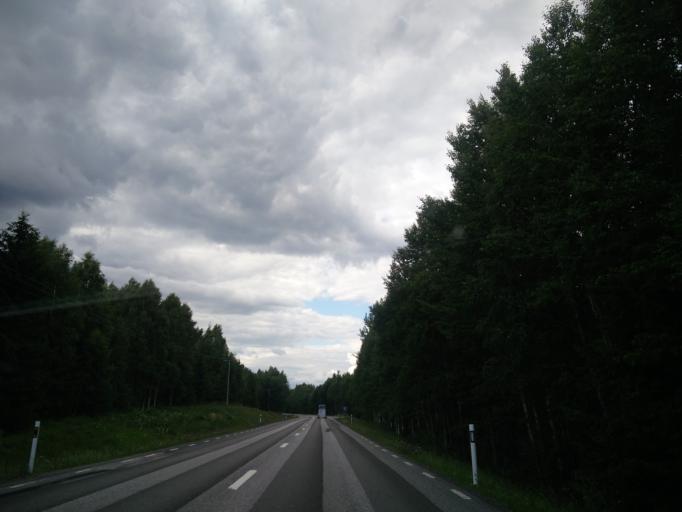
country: SE
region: OErebro
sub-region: Hallefors Kommun
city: Haellefors
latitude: 59.7795
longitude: 14.3854
